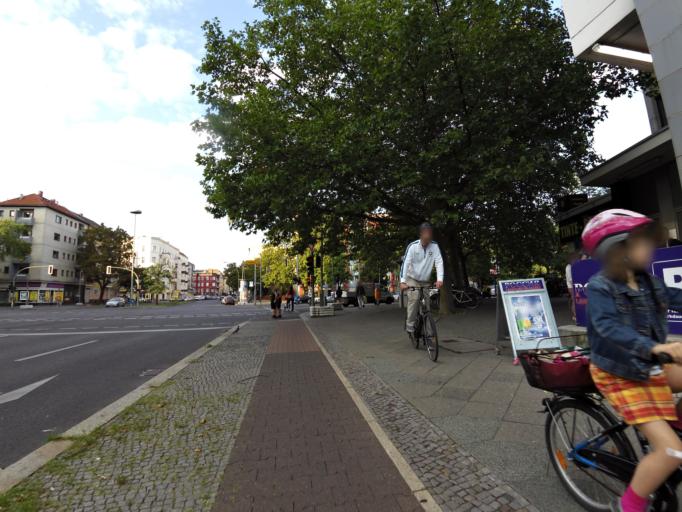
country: DE
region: Berlin
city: Berlin Schoeneberg
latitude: 52.4990
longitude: 13.3351
